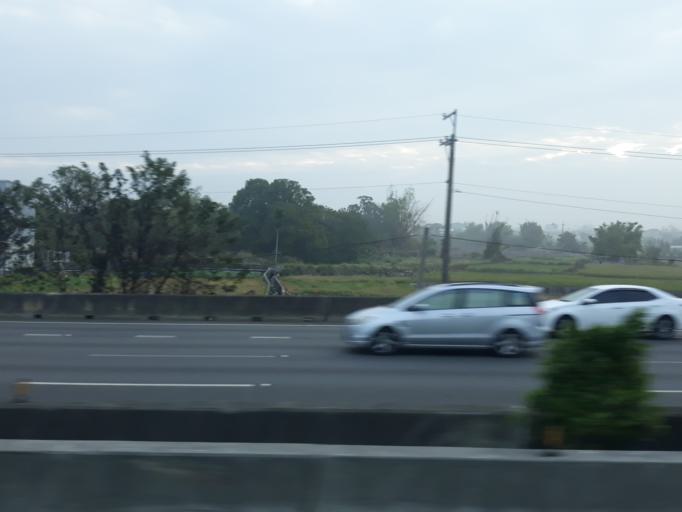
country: TW
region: Taiwan
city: Fengyuan
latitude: 24.2630
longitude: 120.6919
